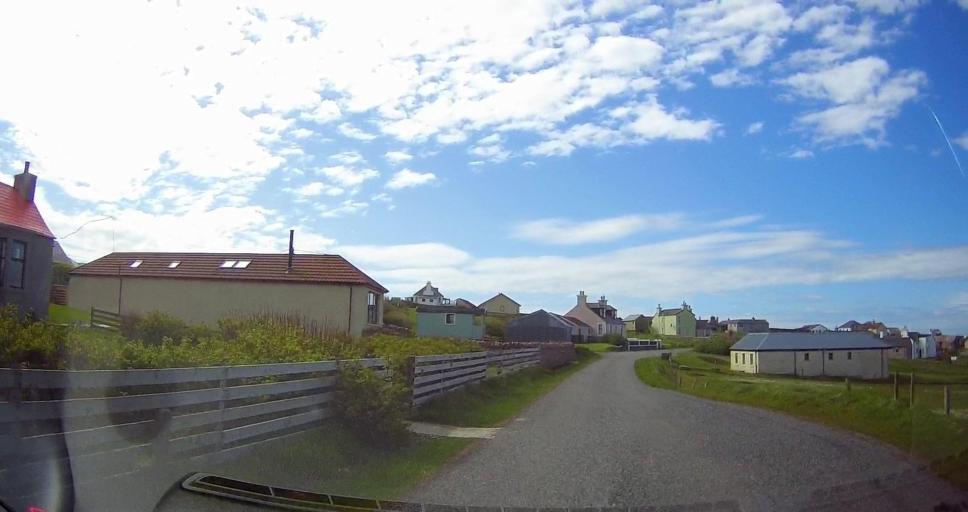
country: GB
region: Scotland
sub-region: Shetland Islands
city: Sandwick
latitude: 59.9748
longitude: -1.3221
